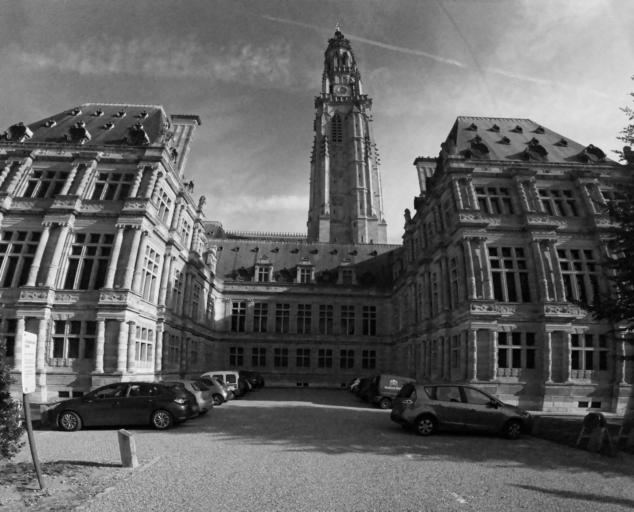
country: FR
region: Nord-Pas-de-Calais
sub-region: Departement du Pas-de-Calais
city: Arras
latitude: 50.2913
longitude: 2.7766
